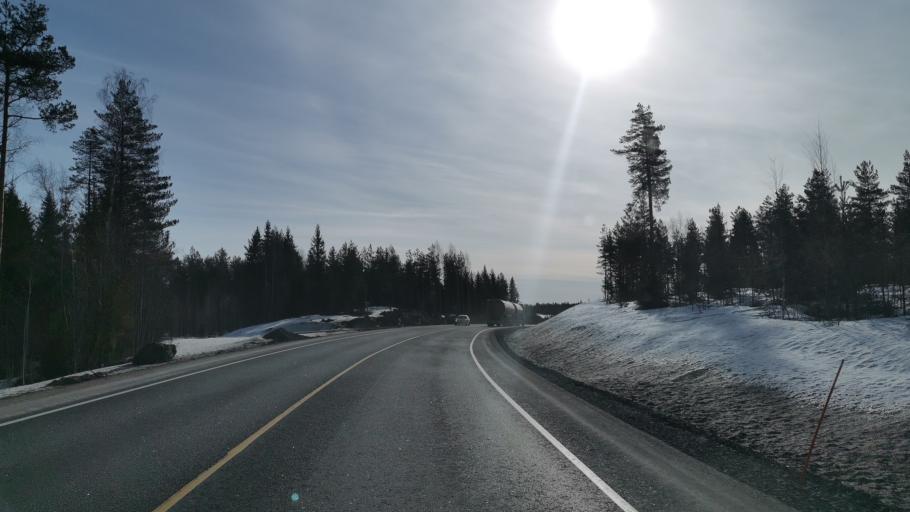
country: FI
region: Kymenlaakso
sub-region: Kouvola
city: Elimaeki
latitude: 60.8717
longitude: 26.5266
